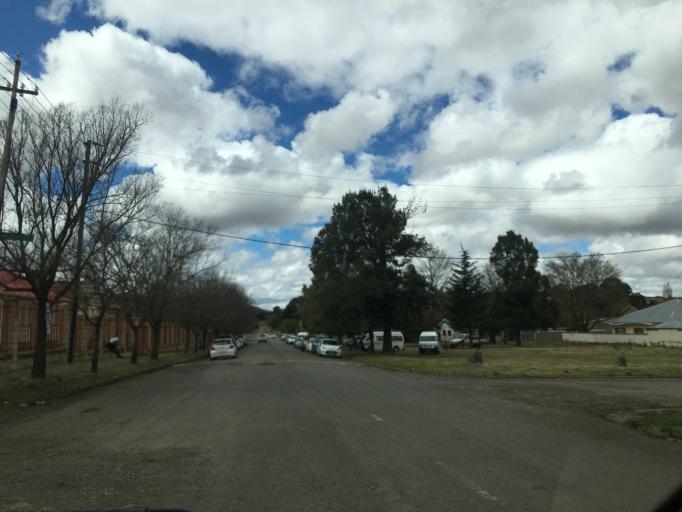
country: ZA
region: Eastern Cape
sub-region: Chris Hani District Municipality
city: Elliot
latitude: -31.3305
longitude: 27.8505
